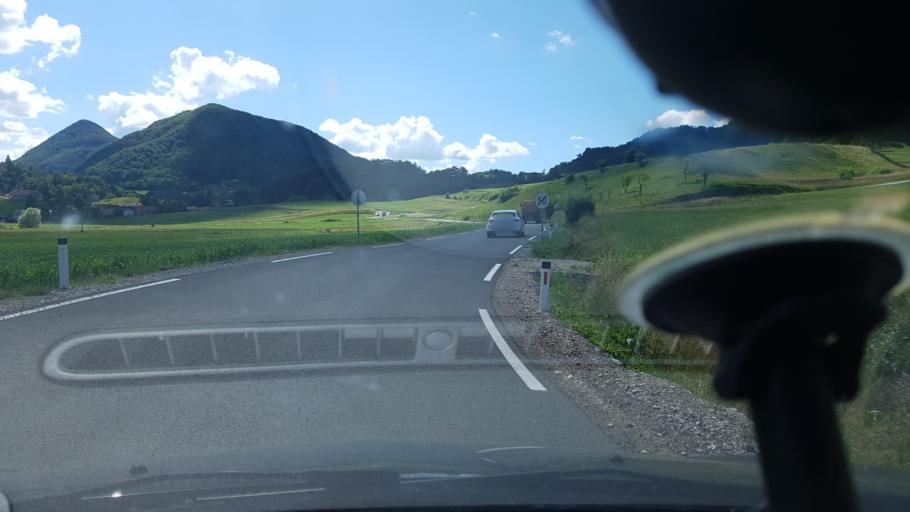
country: SI
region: Zetale
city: Zetale
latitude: 46.2771
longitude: 15.8024
